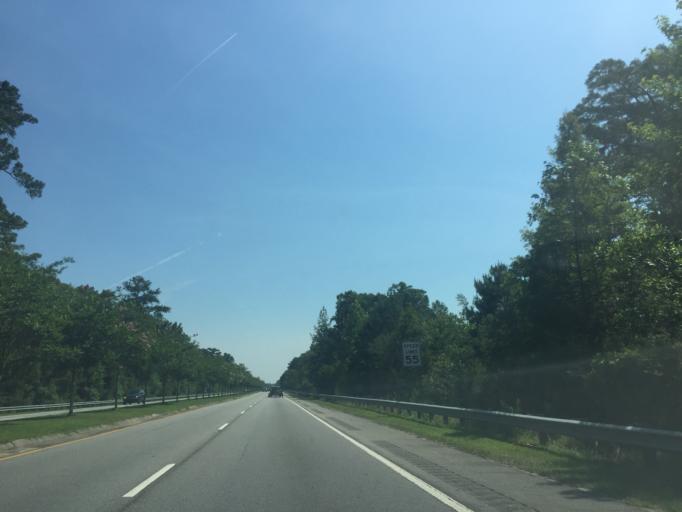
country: US
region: Georgia
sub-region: Bryan County
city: Richmond Hill
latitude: 31.9619
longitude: -81.3027
